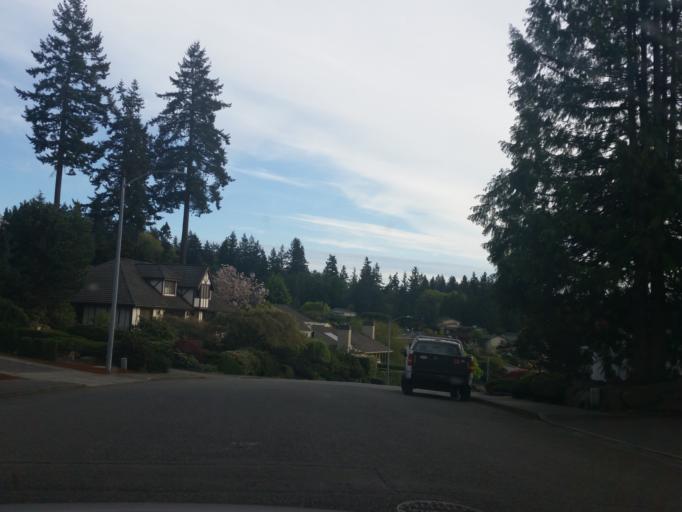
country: US
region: Washington
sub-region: Snohomish County
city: Edmonds
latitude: 47.8140
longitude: -122.3585
